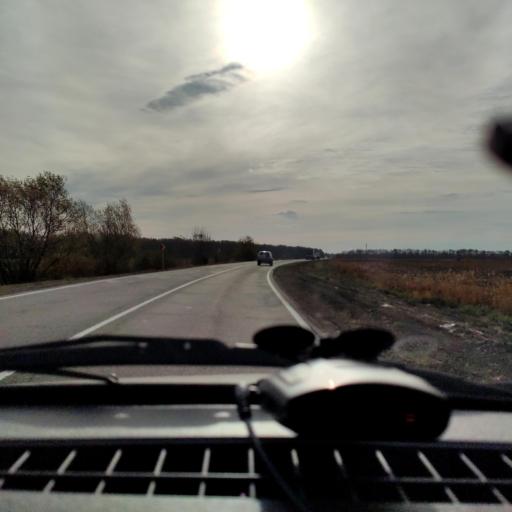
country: RU
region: Voronezj
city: Shilovo
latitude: 51.4500
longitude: 38.9900
